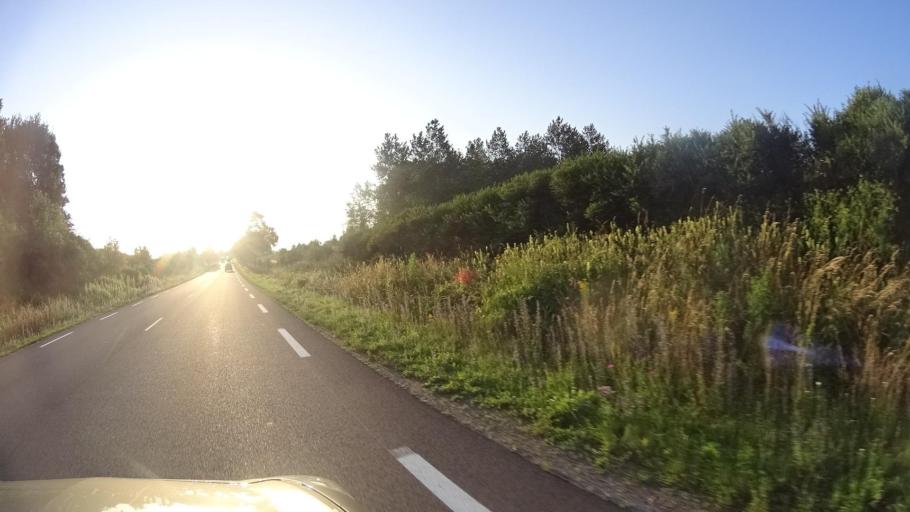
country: FR
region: Franche-Comte
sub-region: Departement du Doubs
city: Doubs
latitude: 46.9111
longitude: 6.2760
